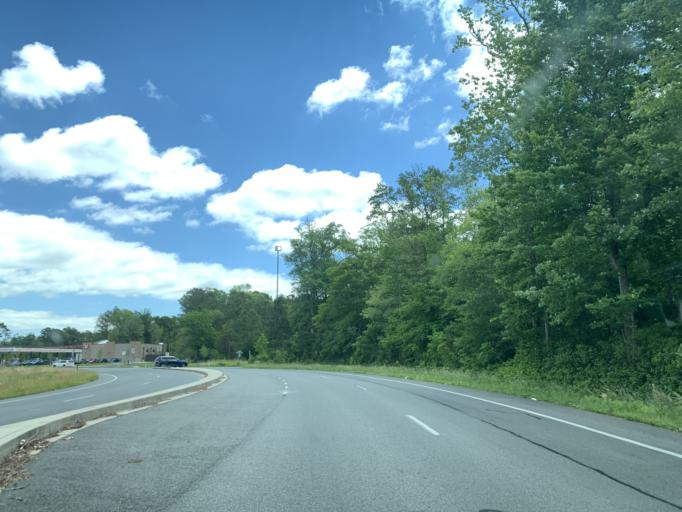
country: US
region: Maryland
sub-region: Worcester County
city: West Ocean City
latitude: 38.3398
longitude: -75.1572
